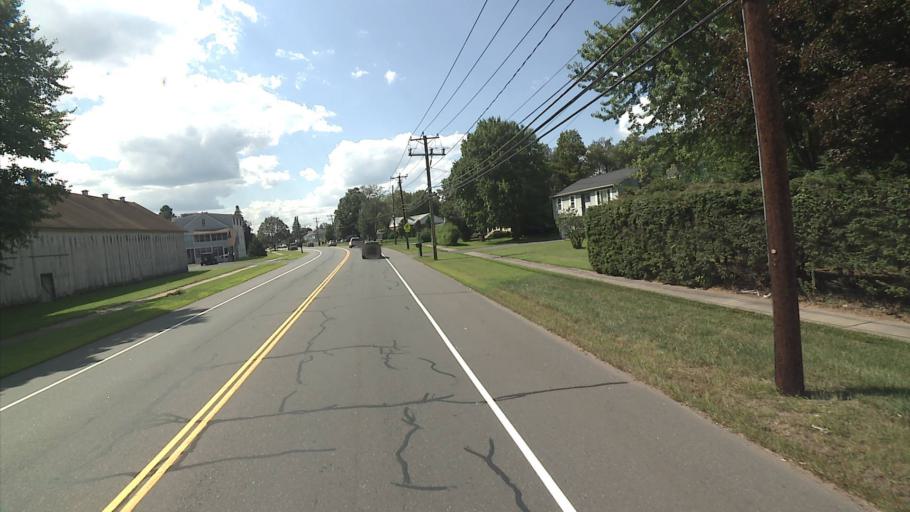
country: US
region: Connecticut
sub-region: Hartford County
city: Hazardville
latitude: 41.9862
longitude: -72.5283
